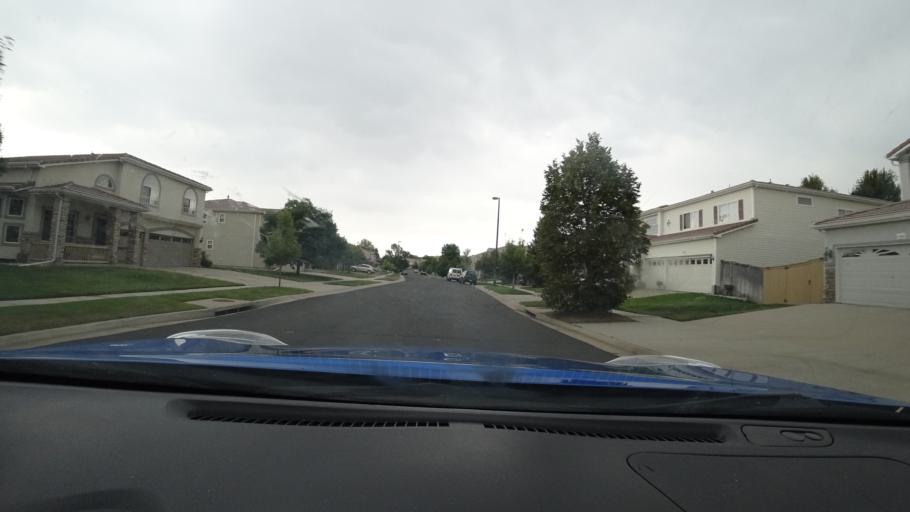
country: US
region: Colorado
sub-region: Adams County
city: Aurora
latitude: 39.7839
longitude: -104.7505
